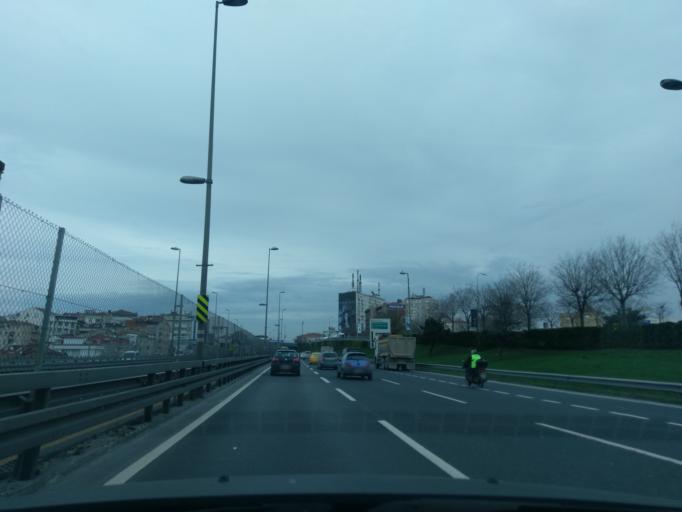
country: TR
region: Istanbul
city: Sisli
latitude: 41.0610
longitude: 28.9666
